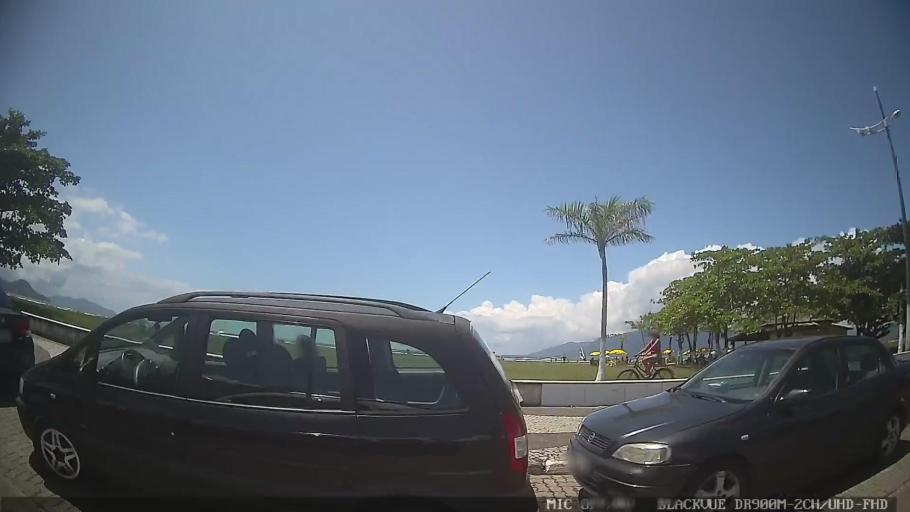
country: BR
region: Sao Paulo
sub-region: Caraguatatuba
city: Caraguatatuba
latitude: -23.6696
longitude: -45.4314
